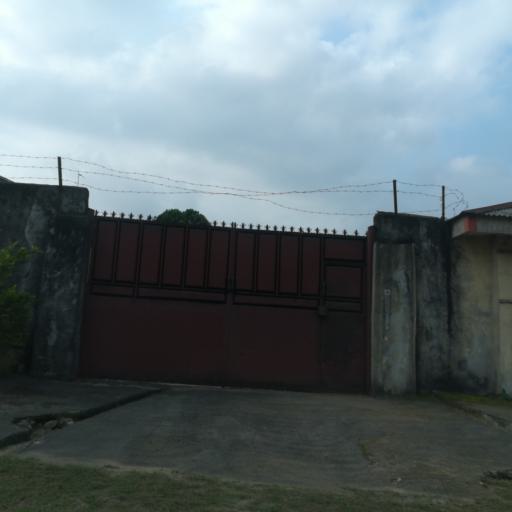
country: NG
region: Rivers
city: Okrika
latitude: 4.7828
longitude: 7.1447
